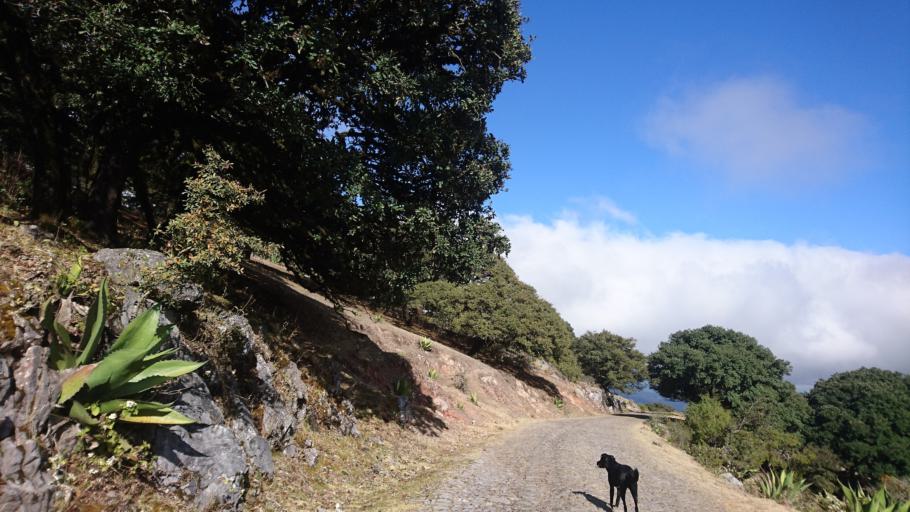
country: MX
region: San Luis Potosi
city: Zaragoza
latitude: 22.0654
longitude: -100.6416
